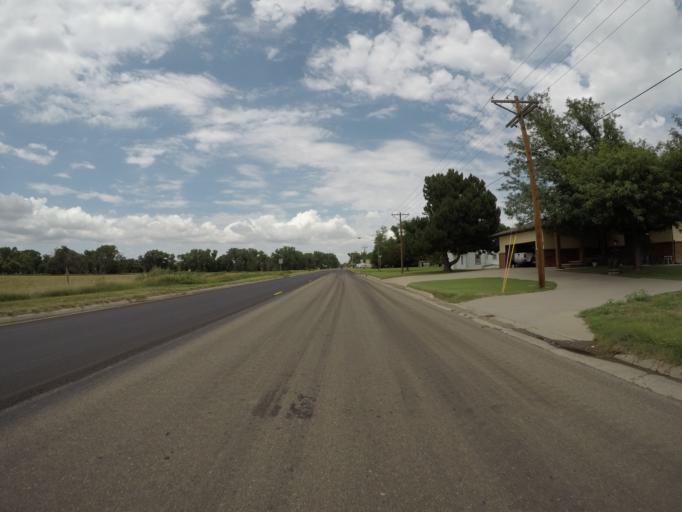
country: US
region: Kansas
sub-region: Rawlins County
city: Atwood
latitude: 39.8050
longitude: -101.0469
